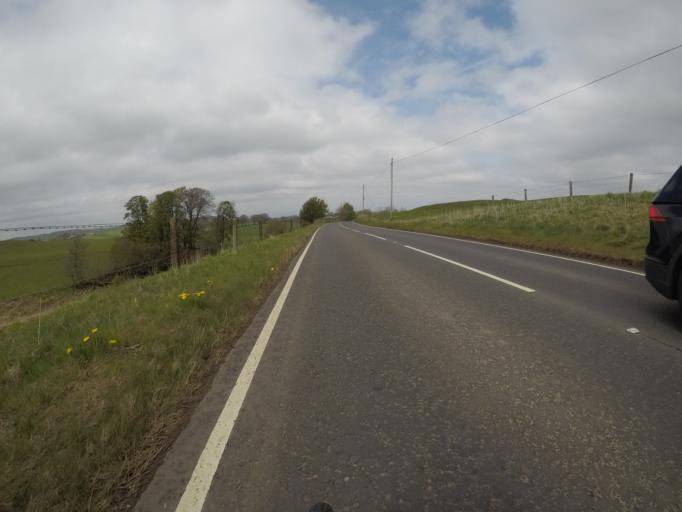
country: GB
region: Scotland
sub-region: East Renfrewshire
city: Barrhead
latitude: 55.7580
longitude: -4.3819
